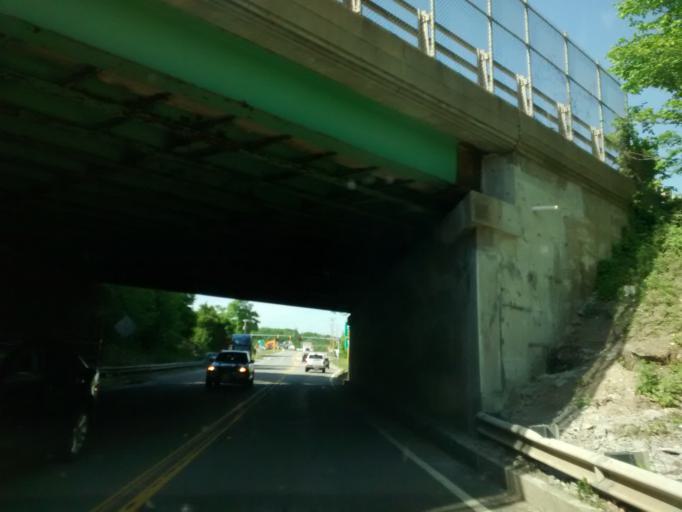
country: US
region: Massachusetts
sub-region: Worcester County
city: Shrewsbury
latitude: 42.2824
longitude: -71.6703
